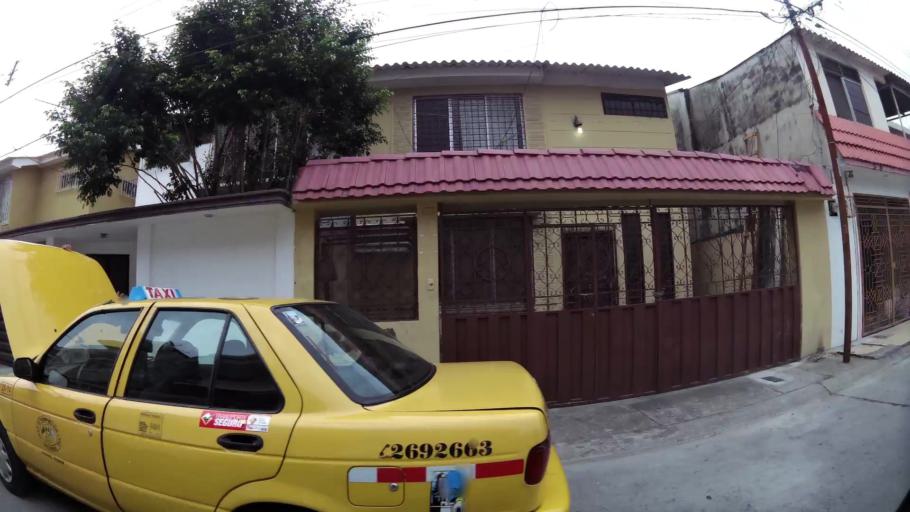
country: EC
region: Guayas
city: Eloy Alfaro
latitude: -2.1409
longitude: -79.8858
